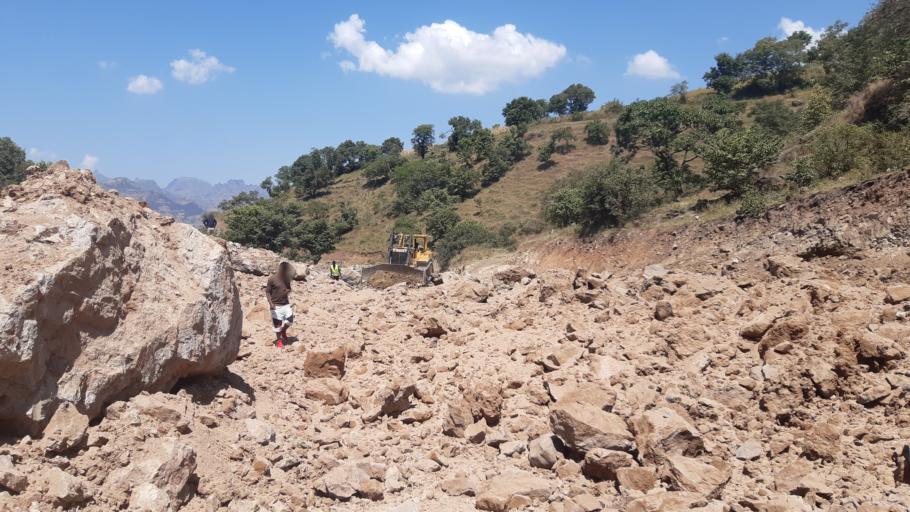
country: ET
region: Amhara
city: Dabat
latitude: 13.1770
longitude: 37.5975
